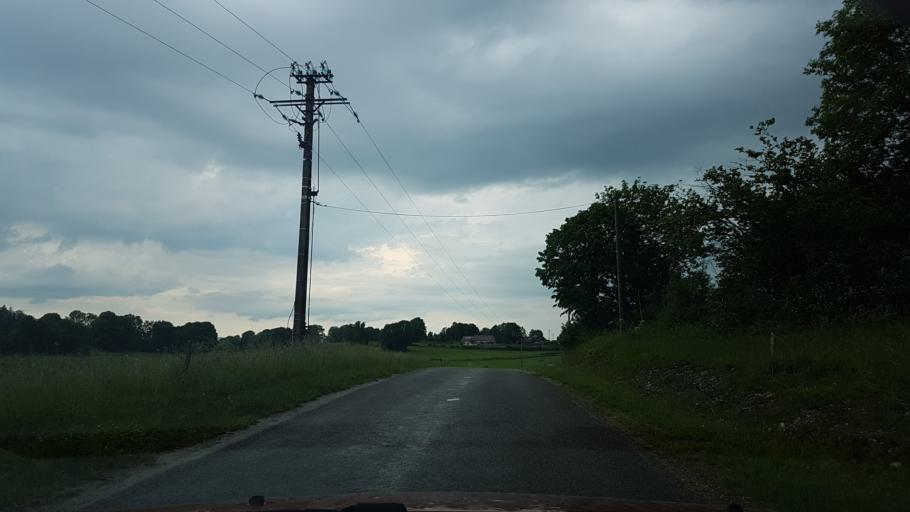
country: FR
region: Franche-Comte
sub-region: Departement du Jura
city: Clairvaux-les-Lacs
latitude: 46.5385
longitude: 5.7439
